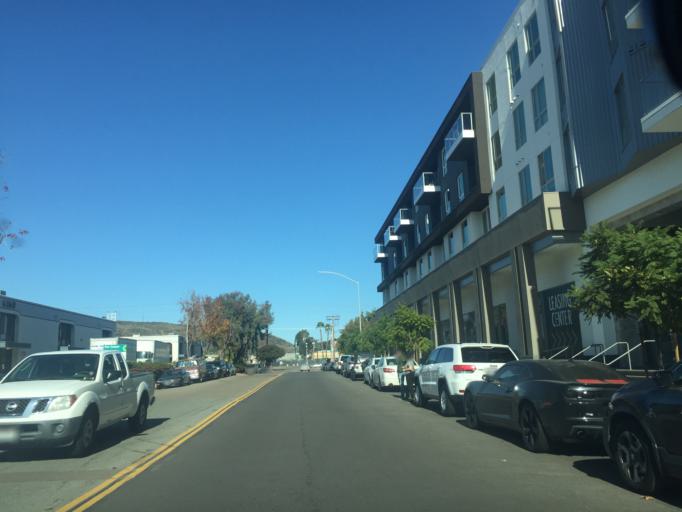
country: US
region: California
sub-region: San Diego County
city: La Mesa
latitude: 32.7861
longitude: -117.1015
